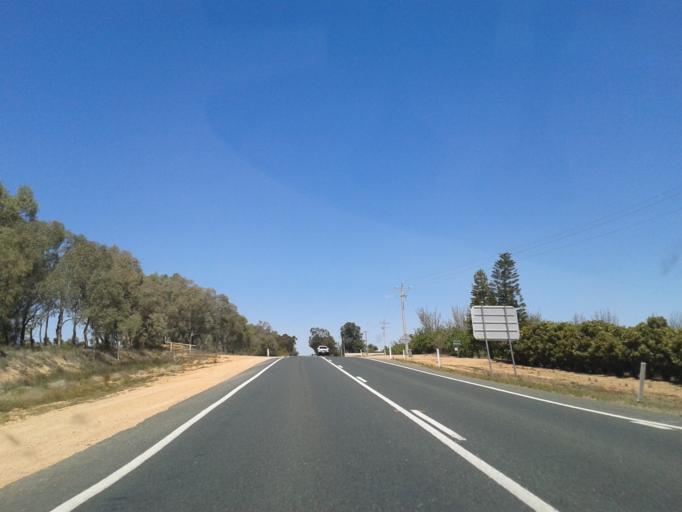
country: AU
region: New South Wales
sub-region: Wentworth
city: Gol Gol
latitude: -34.2413
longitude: 142.2493
